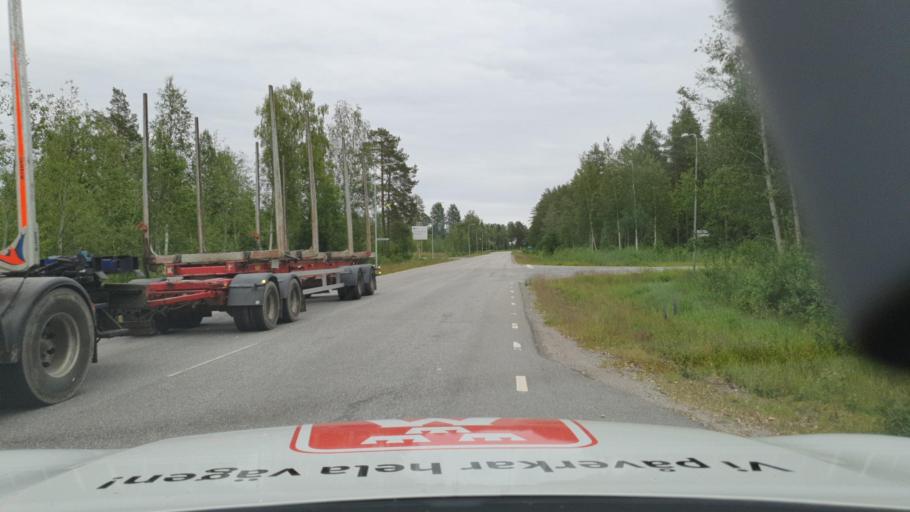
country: SE
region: Vaesterbotten
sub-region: Nordmalings Kommun
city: Nordmaling
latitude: 63.5476
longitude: 19.4271
